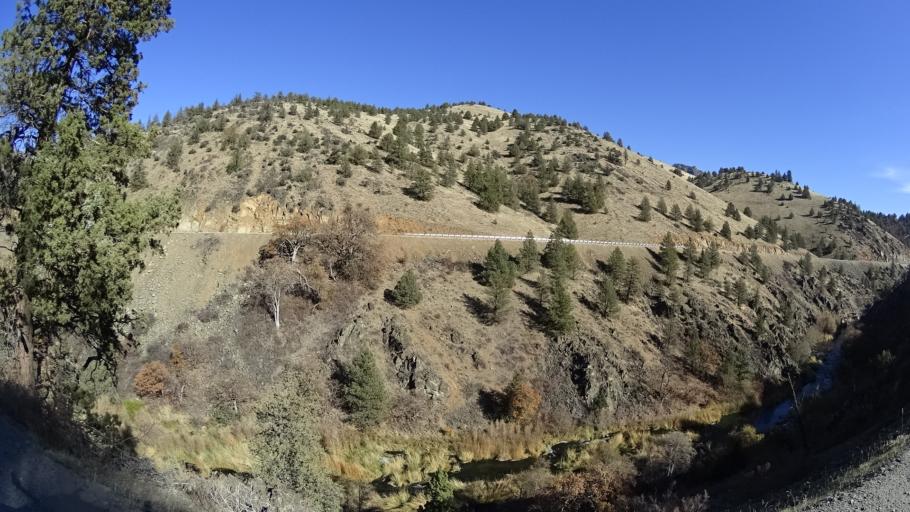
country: US
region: California
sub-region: Siskiyou County
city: Yreka
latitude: 41.7897
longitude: -122.6077
